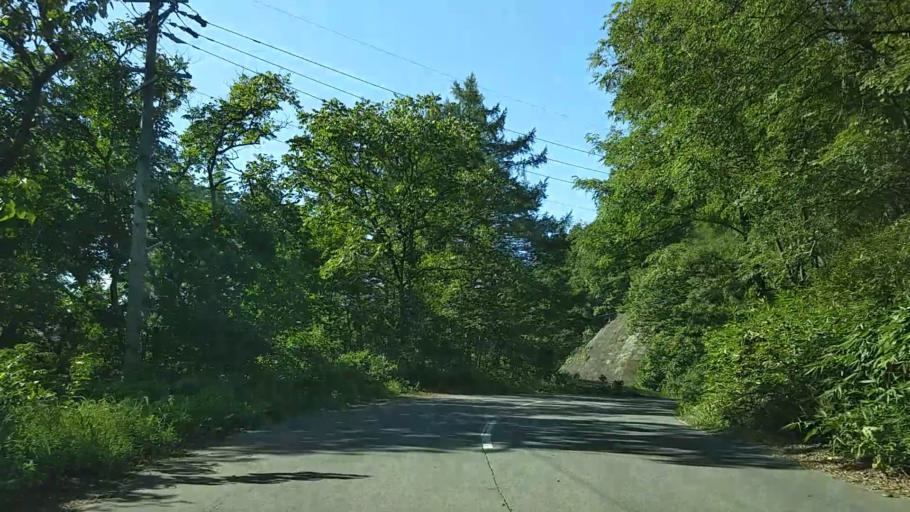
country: JP
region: Nagano
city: Nagano-shi
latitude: 36.6068
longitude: 138.0914
